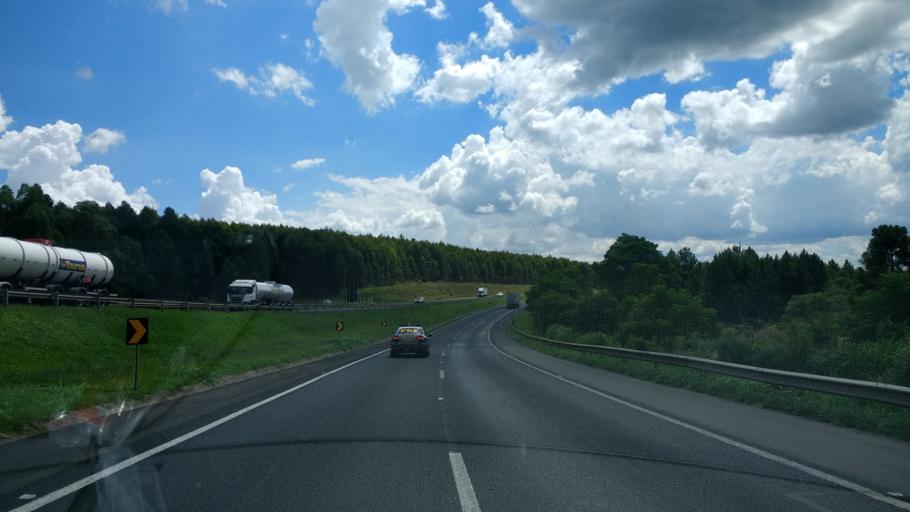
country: BR
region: Parana
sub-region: Palmeira
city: Palmeira
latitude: -25.2704
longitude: -49.9412
